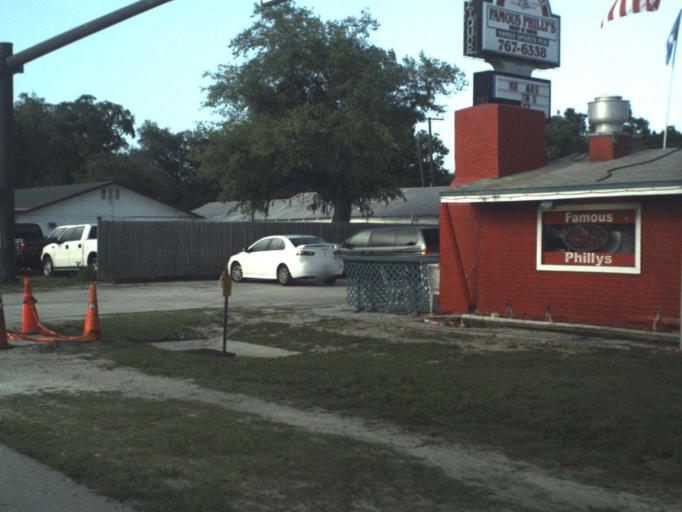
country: US
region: Florida
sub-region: Volusia County
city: Port Orange
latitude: 29.1079
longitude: -80.9731
